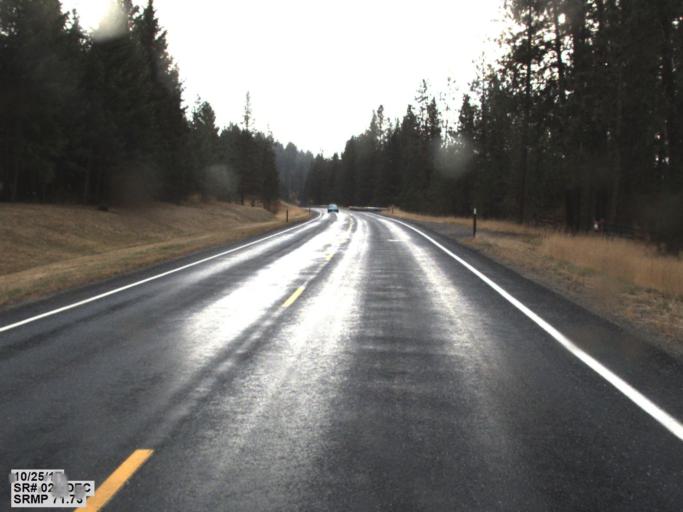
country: US
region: Washington
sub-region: Stevens County
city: Kettle Falls
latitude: 48.4980
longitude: -118.1599
